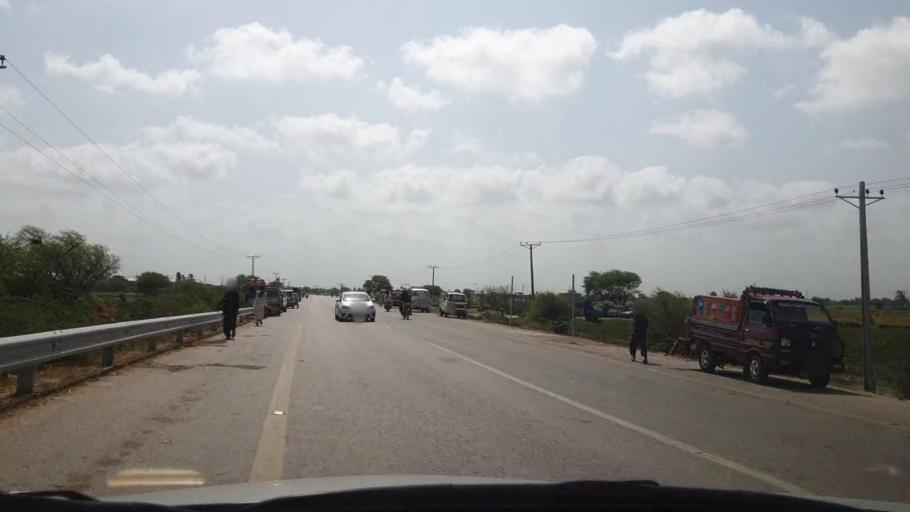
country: PK
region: Sindh
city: Talhar
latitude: 24.8913
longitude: 68.7968
